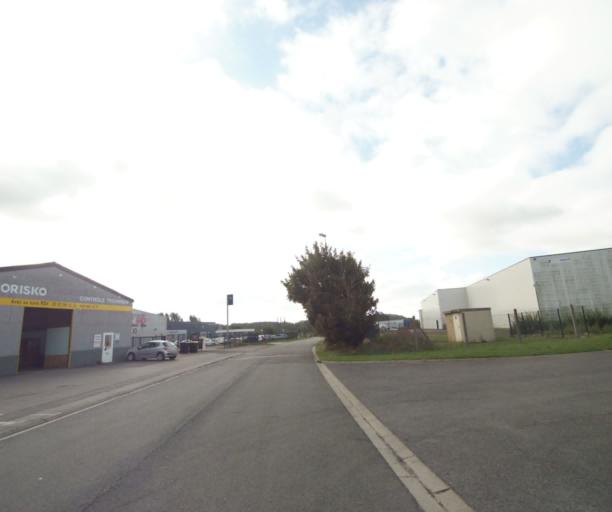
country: FR
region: Nord-Pas-de-Calais
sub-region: Departement du Pas-de-Calais
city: Etaples
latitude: 50.5165
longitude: 1.6653
